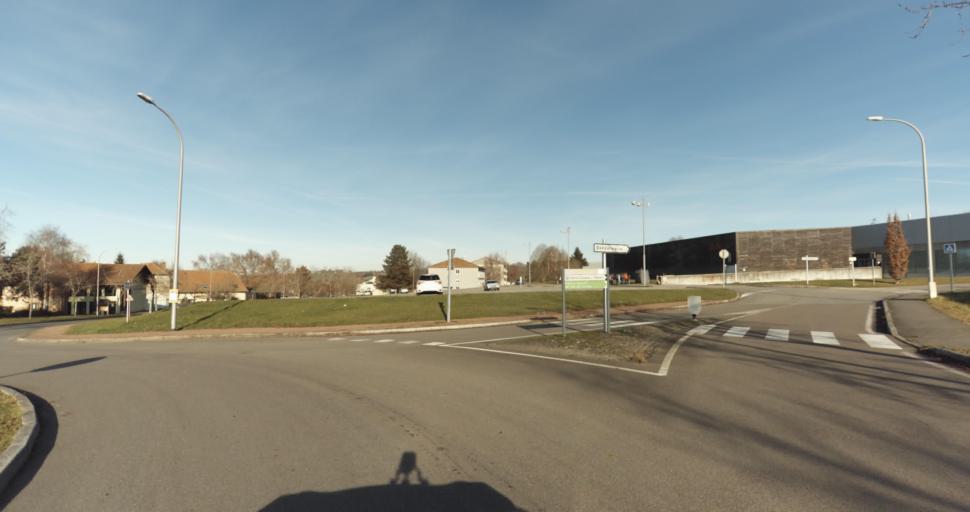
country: FR
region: Limousin
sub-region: Departement de la Haute-Vienne
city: Aixe-sur-Vienne
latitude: 45.7924
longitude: 1.1302
